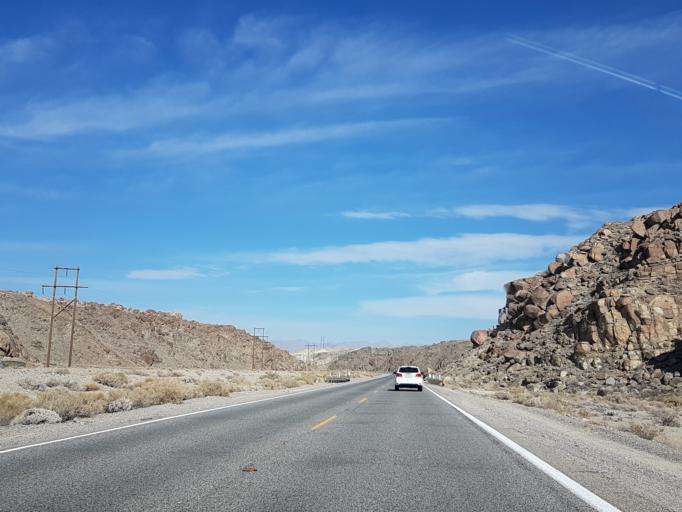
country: US
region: California
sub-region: San Bernardino County
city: Searles Valley
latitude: 35.6606
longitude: -117.4338
